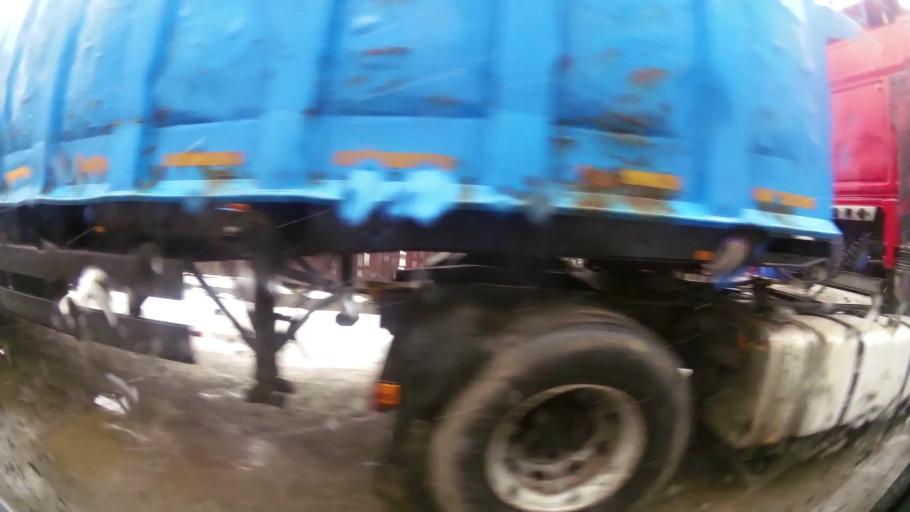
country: RO
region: Ilfov
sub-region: Comuna Chiajna
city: Rosu
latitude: 44.4279
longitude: 26.0073
